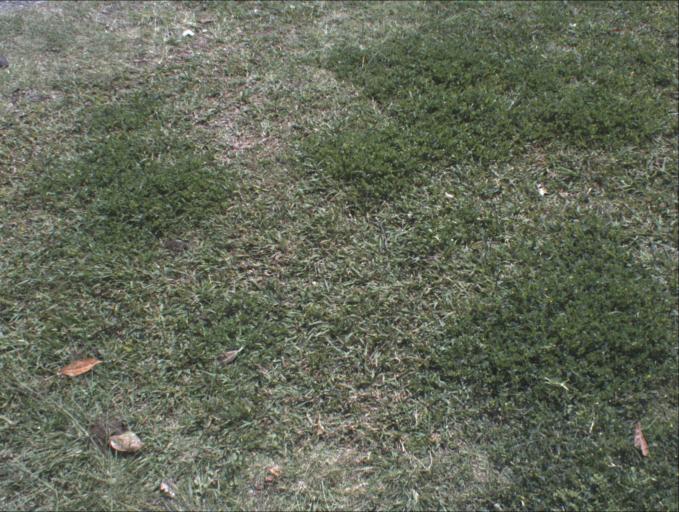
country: AU
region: Queensland
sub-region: Logan
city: Waterford West
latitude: -27.6859
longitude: 153.1578
